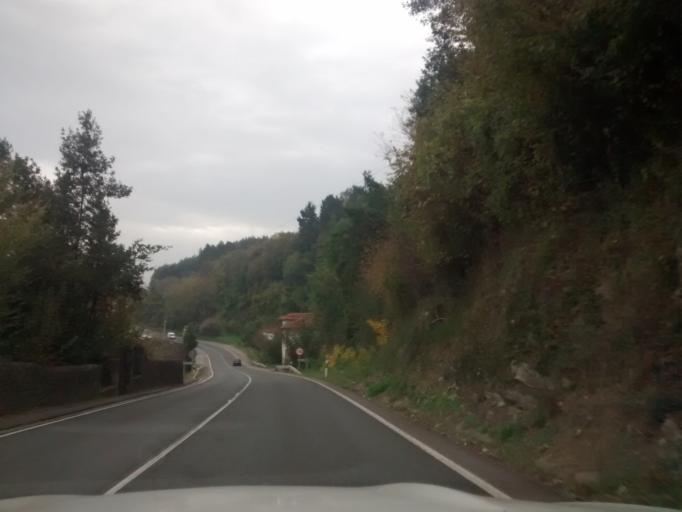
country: ES
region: Cantabria
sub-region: Provincia de Cantabria
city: Corvera
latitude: 43.2559
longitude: -3.9488
